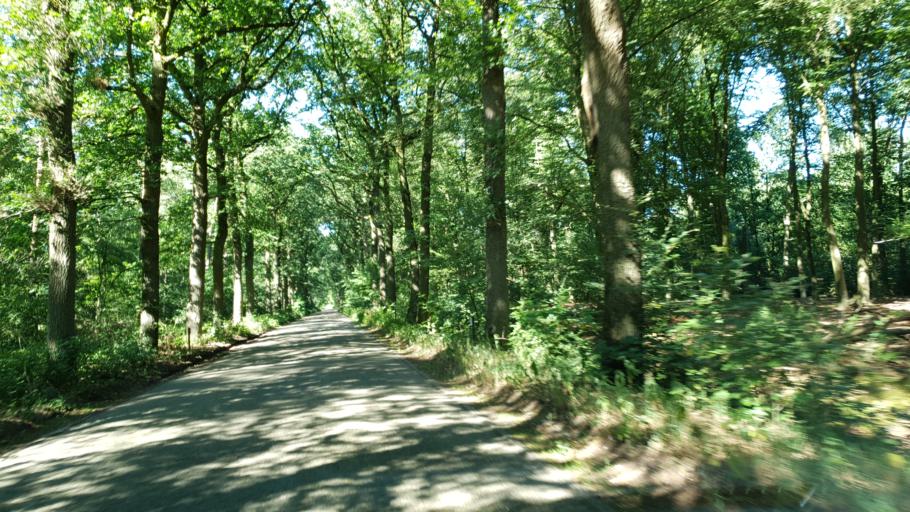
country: BE
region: Flanders
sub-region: Provincie Antwerpen
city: Merksplas
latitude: 51.3750
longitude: 4.8251
